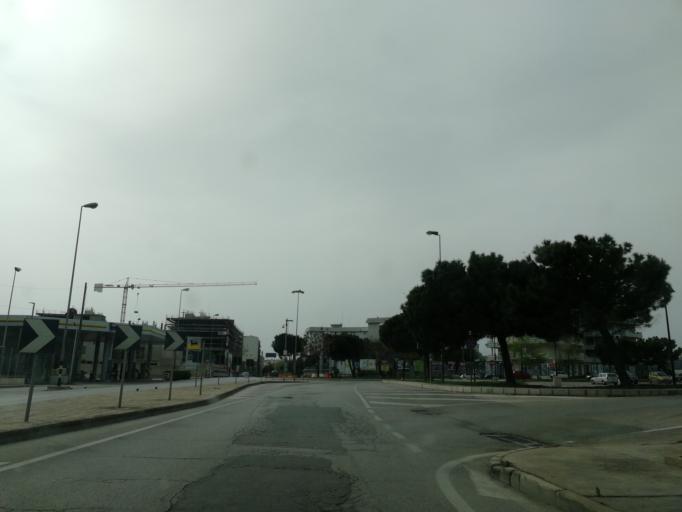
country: IT
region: Apulia
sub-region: Provincia di Barletta - Andria - Trani
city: Barletta
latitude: 41.3178
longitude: 16.2931
